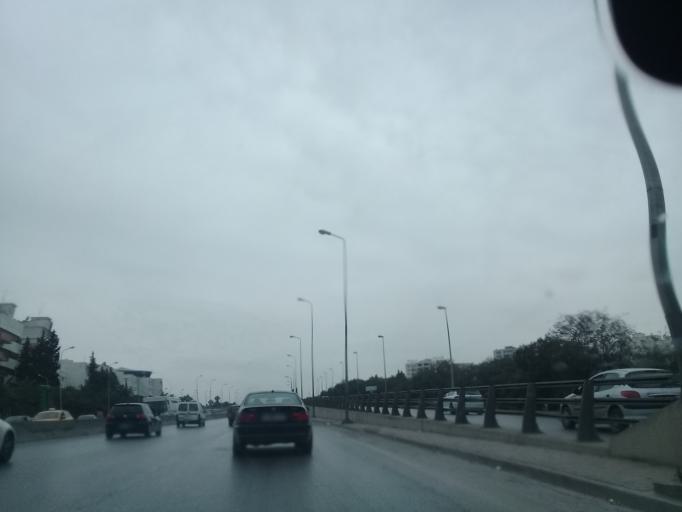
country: TN
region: Tunis
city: Tunis
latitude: 36.8355
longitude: 10.1599
